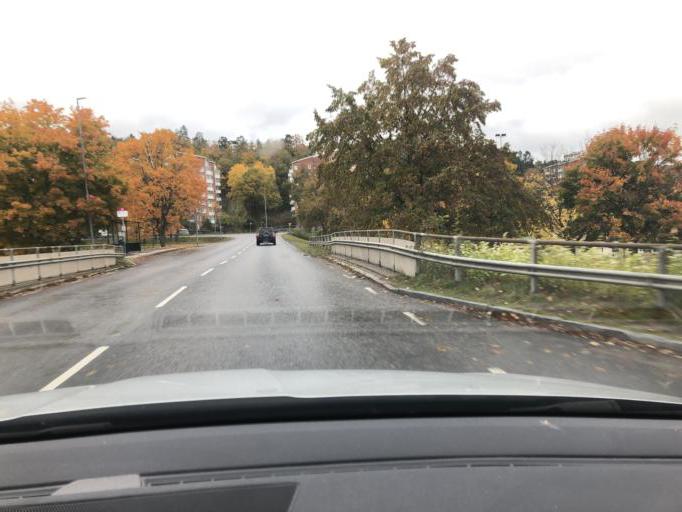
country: SE
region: Stockholm
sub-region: Botkyrka Kommun
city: Alby
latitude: 59.2374
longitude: 17.8519
